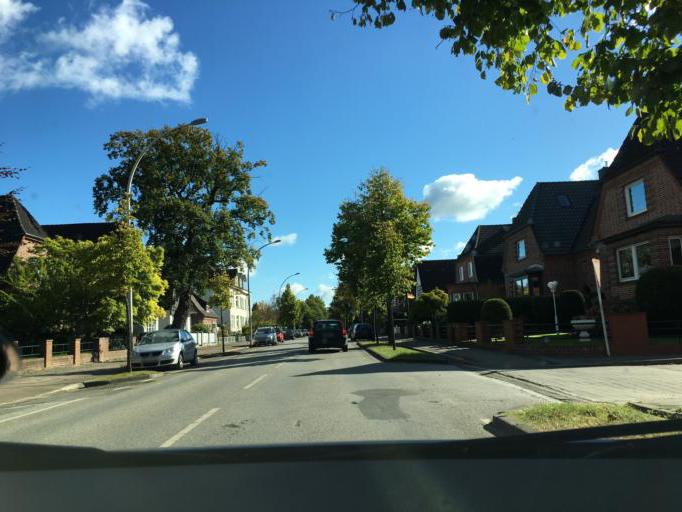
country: DE
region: Schleswig-Holstein
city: Kronshagen
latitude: 54.3294
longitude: 10.0921
